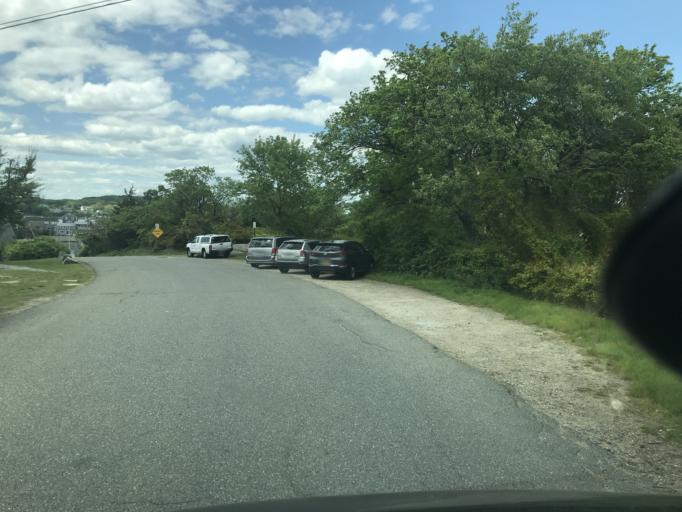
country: US
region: Massachusetts
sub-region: Essex County
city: Rockport
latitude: 42.6586
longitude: -70.6113
